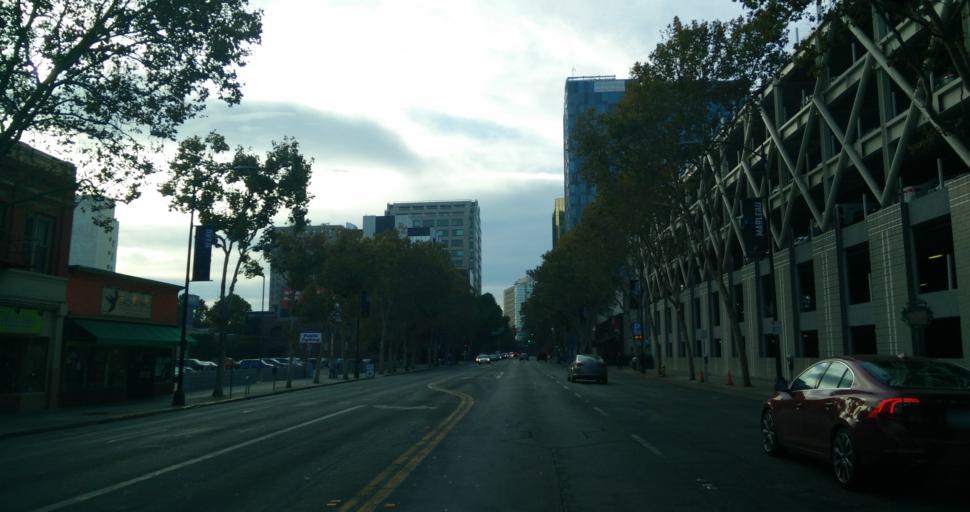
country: US
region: California
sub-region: Santa Clara County
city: San Jose
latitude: 37.3368
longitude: -121.8932
